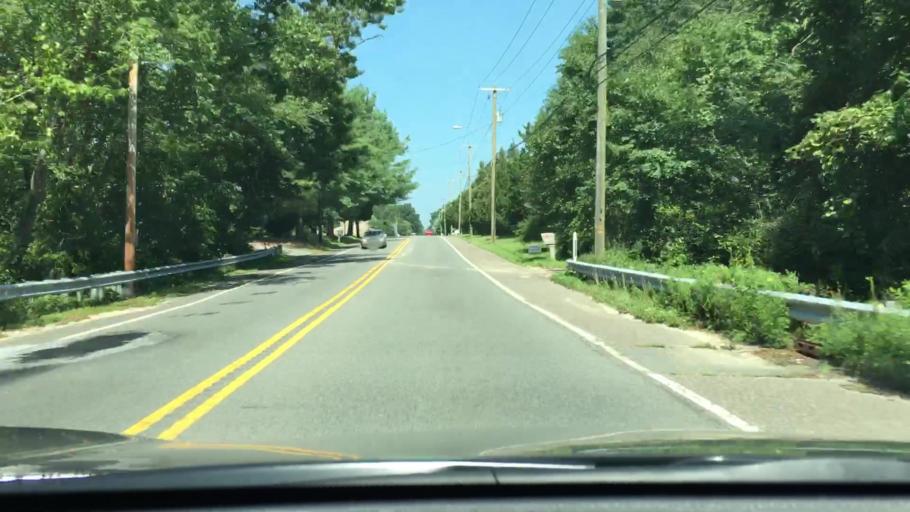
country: US
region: New Jersey
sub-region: Cumberland County
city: Laurel Lake
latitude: 39.3166
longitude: -75.0112
